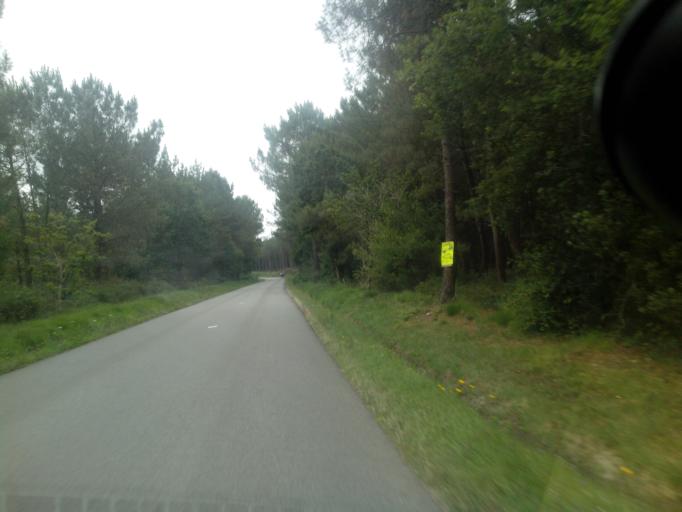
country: FR
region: Brittany
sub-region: Departement du Morbihan
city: Merlevenez
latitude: 47.7193
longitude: -3.2596
